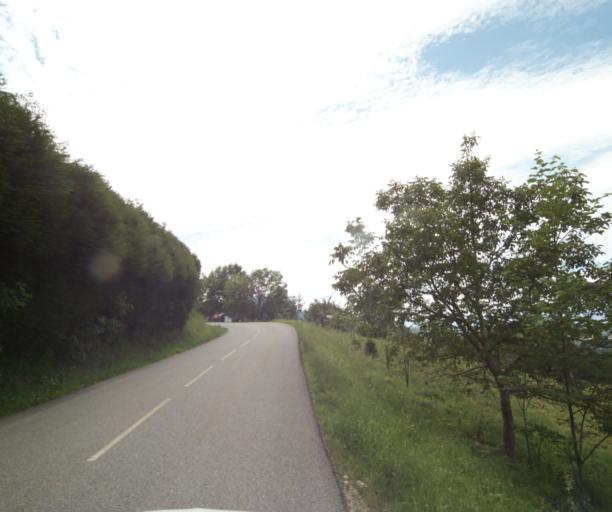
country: FR
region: Rhone-Alpes
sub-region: Departement de la Haute-Savoie
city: Bons-en-Chablais
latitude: 46.2665
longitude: 6.4169
